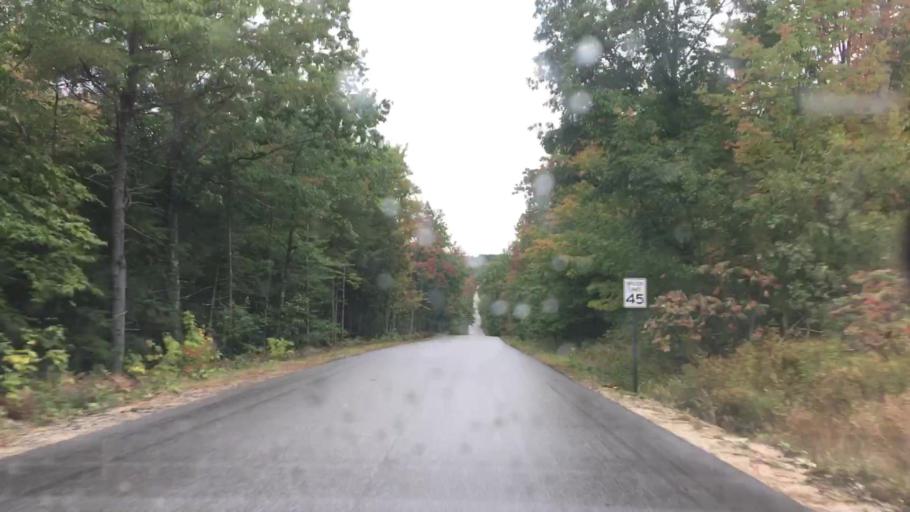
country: US
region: Maine
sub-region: Cumberland County
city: Harrison
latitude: 44.0789
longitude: -70.6421
